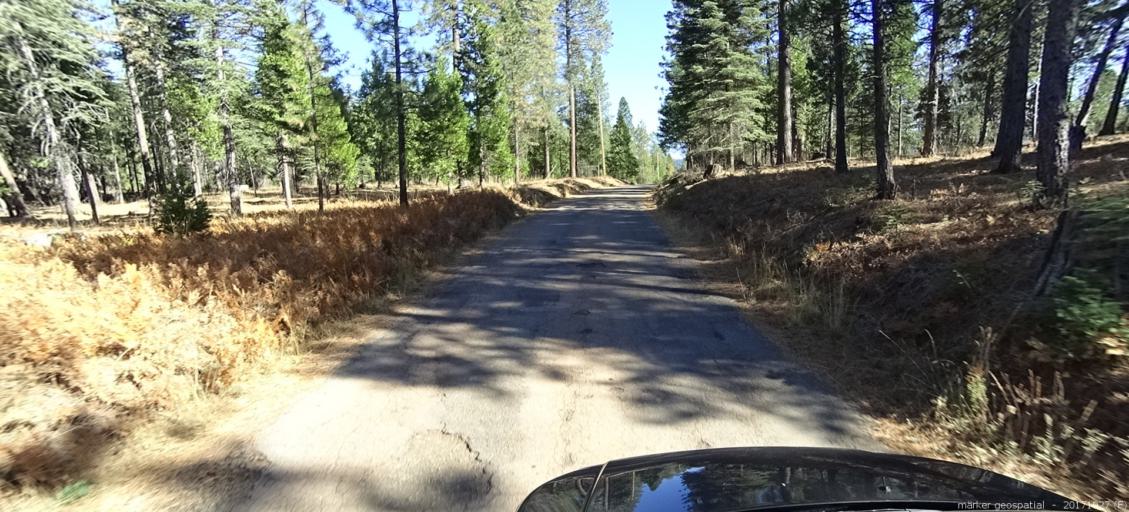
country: US
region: California
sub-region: Shasta County
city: Shingletown
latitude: 40.6142
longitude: -121.8250
